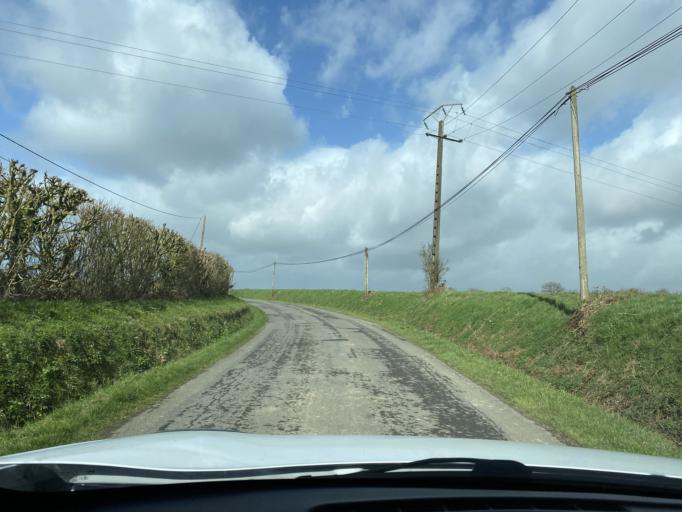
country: FR
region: Brittany
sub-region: Departement d'Ille-et-Vilaine
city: Melesse
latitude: 48.2095
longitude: -1.6834
